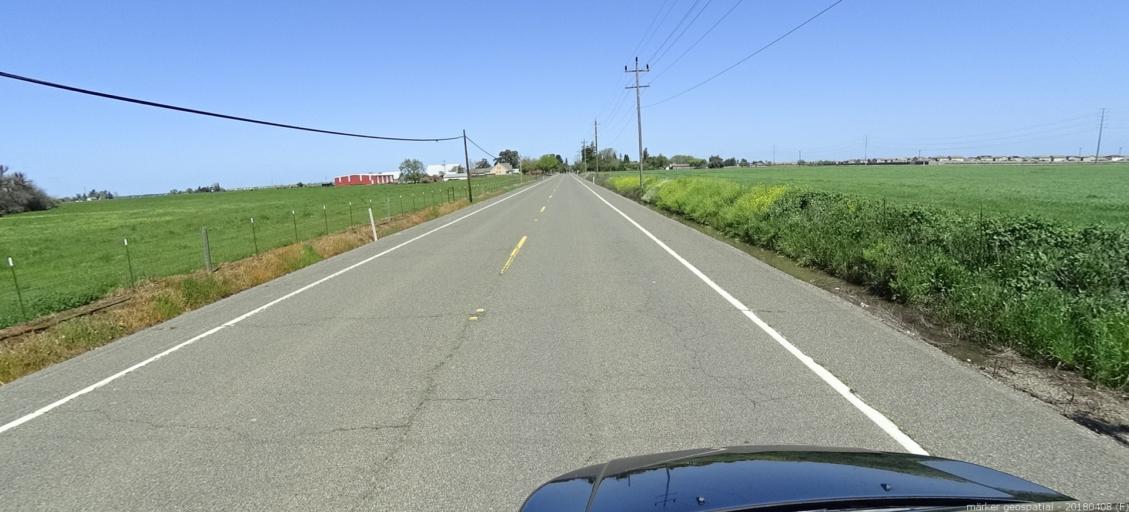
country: US
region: California
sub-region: Sacramento County
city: Laguna
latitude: 38.3675
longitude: -121.4541
